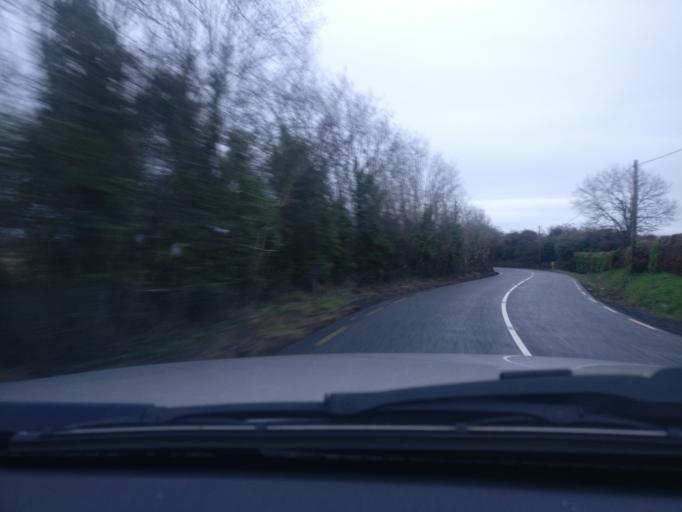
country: IE
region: Leinster
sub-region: Kildare
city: Kilcock
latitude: 53.4541
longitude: -6.6252
